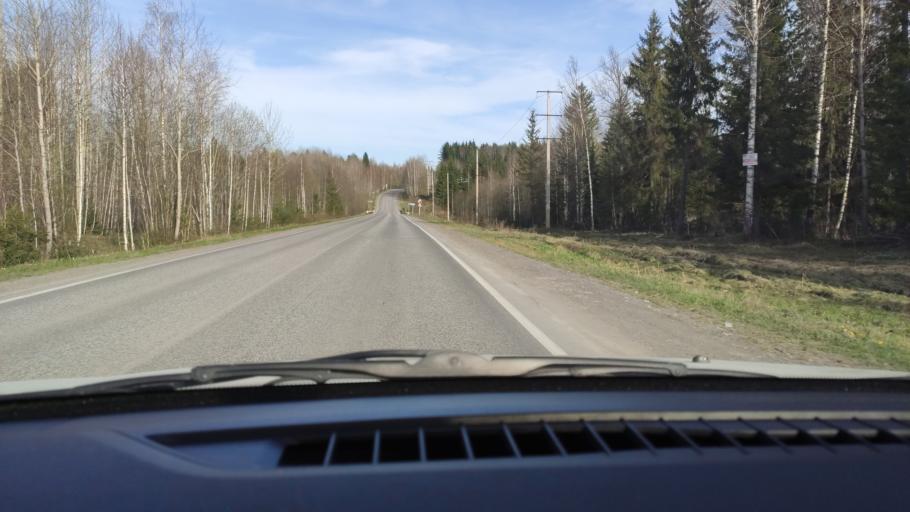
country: RU
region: Perm
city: Novyye Lyady
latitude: 57.9583
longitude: 56.5533
